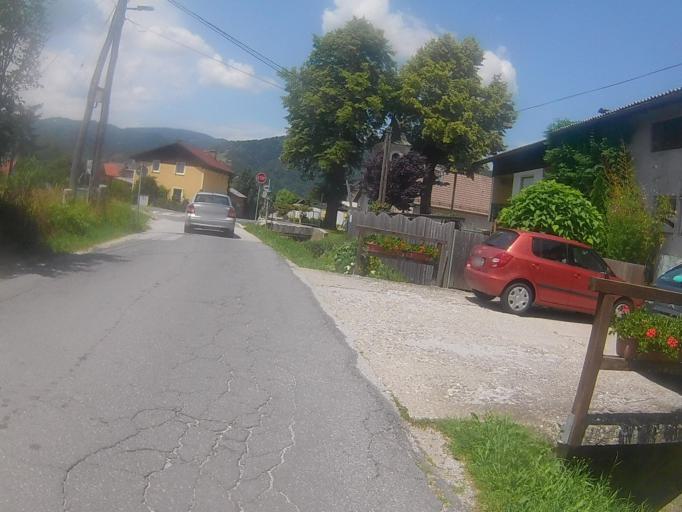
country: SI
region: Ruse
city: Bistrica ob Dravi
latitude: 46.5483
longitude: 15.5357
